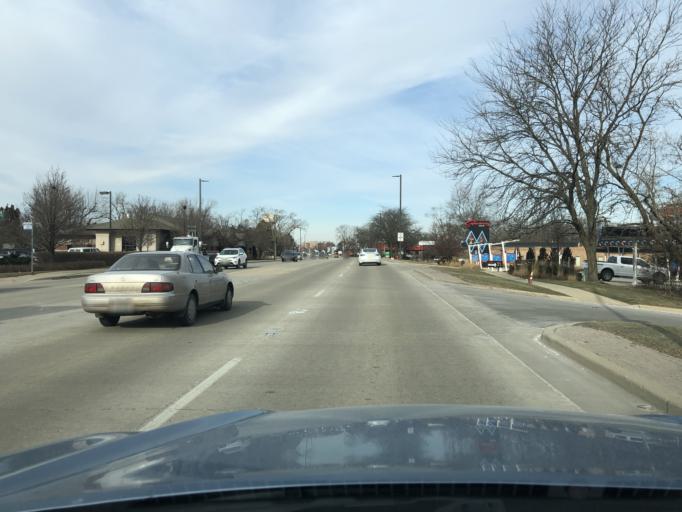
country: US
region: Illinois
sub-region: Cook County
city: Wheeling
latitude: 42.1348
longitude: -87.9028
